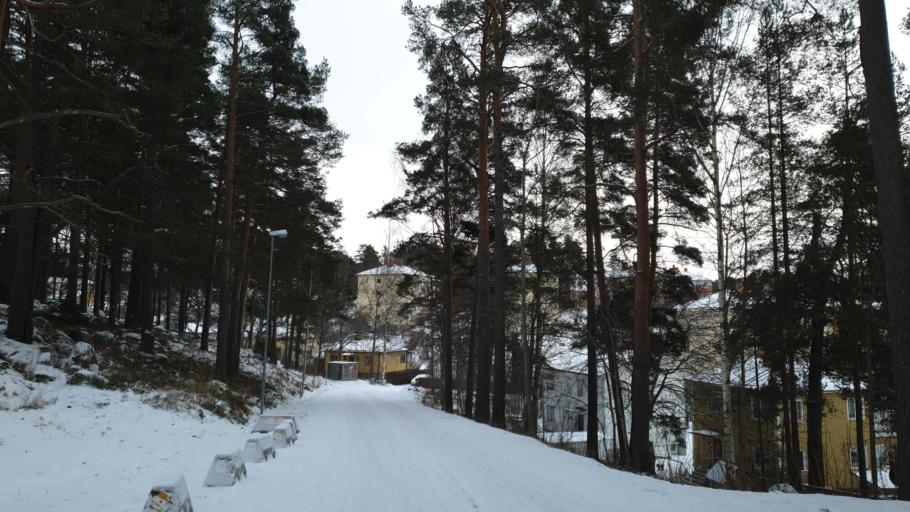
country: SE
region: Gaevleborg
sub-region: Soderhamns Kommun
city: Soderhamn
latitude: 61.3001
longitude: 17.0579
